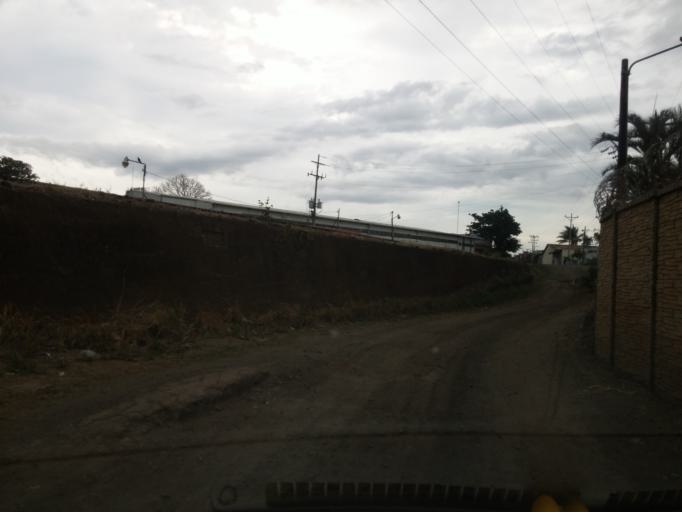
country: CR
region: Alajuela
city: Alajuela
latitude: 10.0022
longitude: -84.1980
